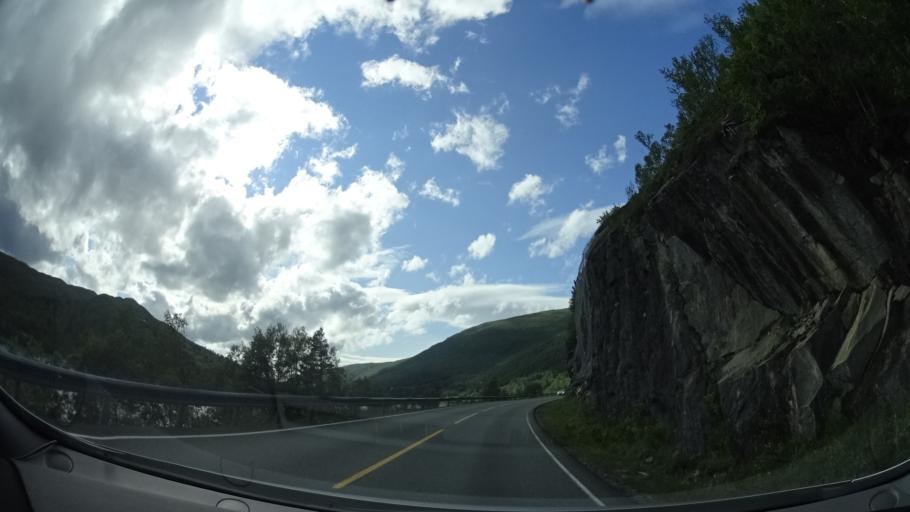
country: NO
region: More og Romsdal
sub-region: Rindal
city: Rindal
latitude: 63.2212
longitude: 9.2632
